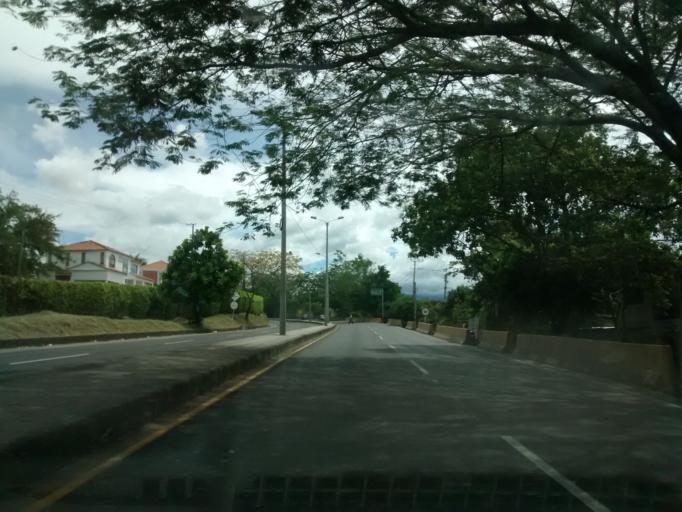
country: CO
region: Tolima
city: Ibague
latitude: 4.4043
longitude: -75.1561
